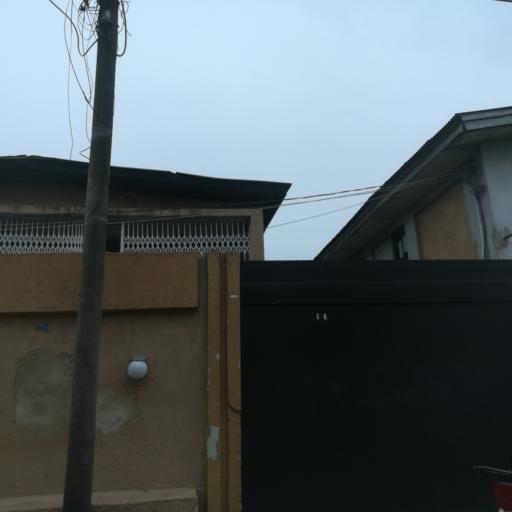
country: NG
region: Lagos
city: Makoko
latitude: 6.5048
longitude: 3.3882
